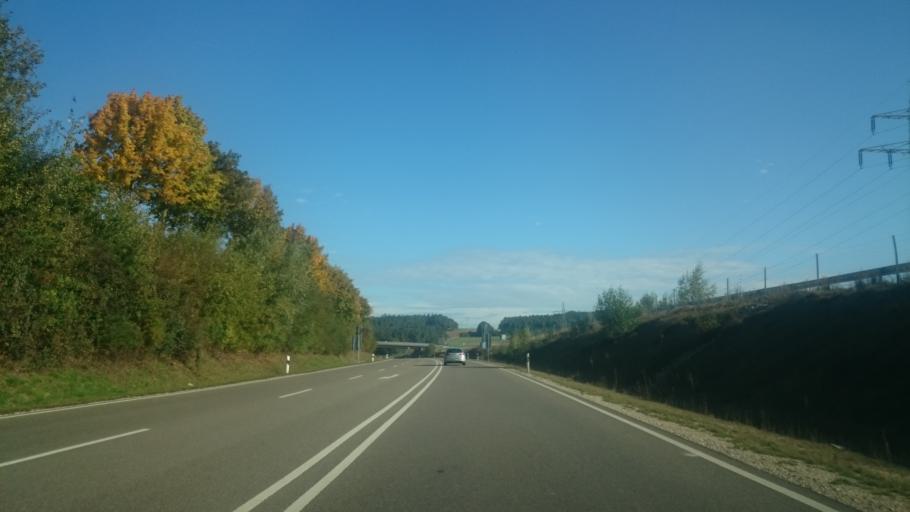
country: DE
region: Bavaria
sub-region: Regierungsbezirk Mittelfranken
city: Pleinfeld
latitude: 49.0969
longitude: 10.9903
